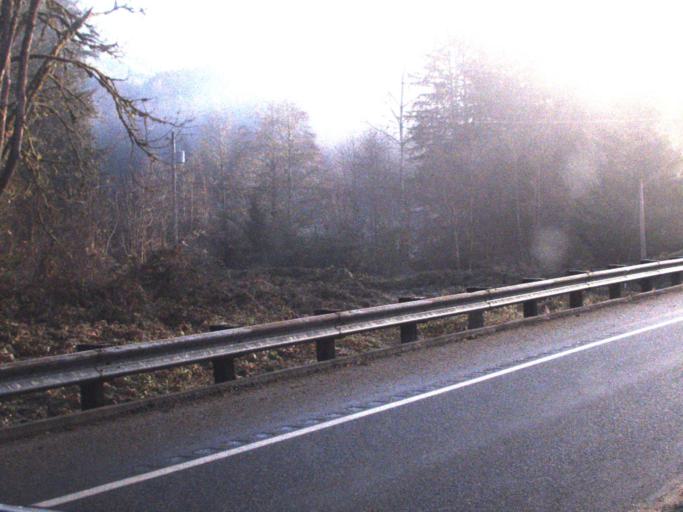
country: US
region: Washington
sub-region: Snohomish County
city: Darrington
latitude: 48.5055
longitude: -121.6534
